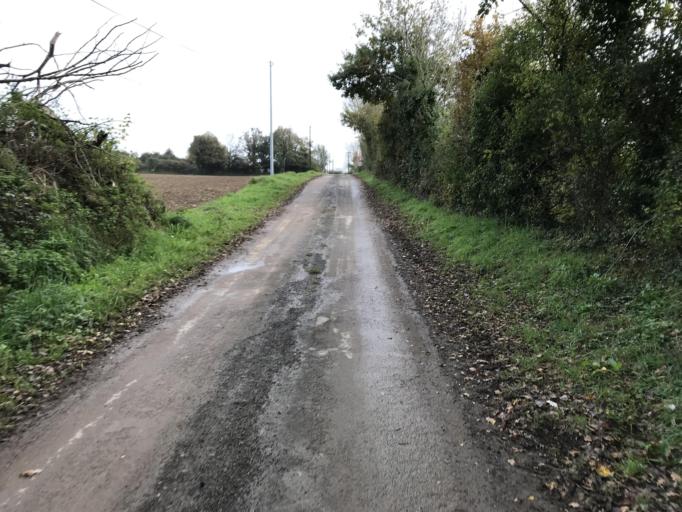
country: FR
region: Brittany
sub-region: Departement du Finistere
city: Hopital-Camfrout
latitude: 48.3276
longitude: -4.2055
